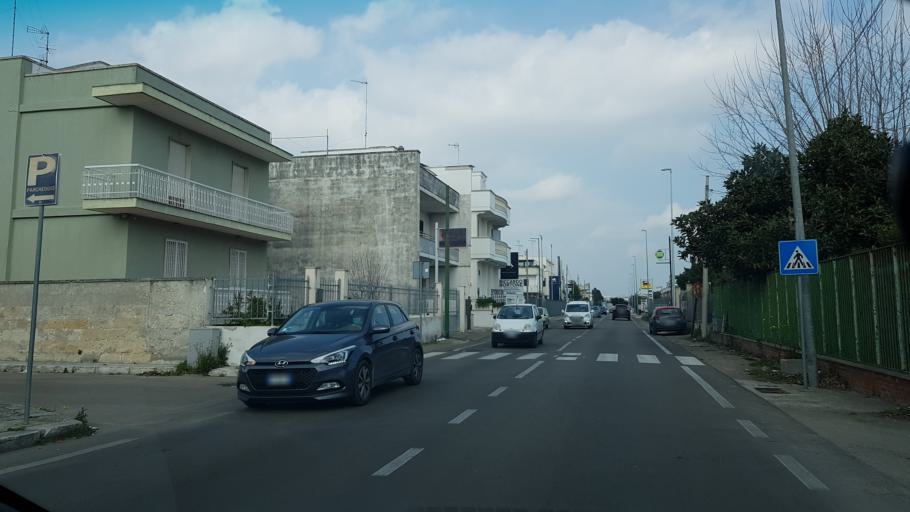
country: IT
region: Apulia
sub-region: Provincia di Lecce
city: Castromediano
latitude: 40.3270
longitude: 18.1823
